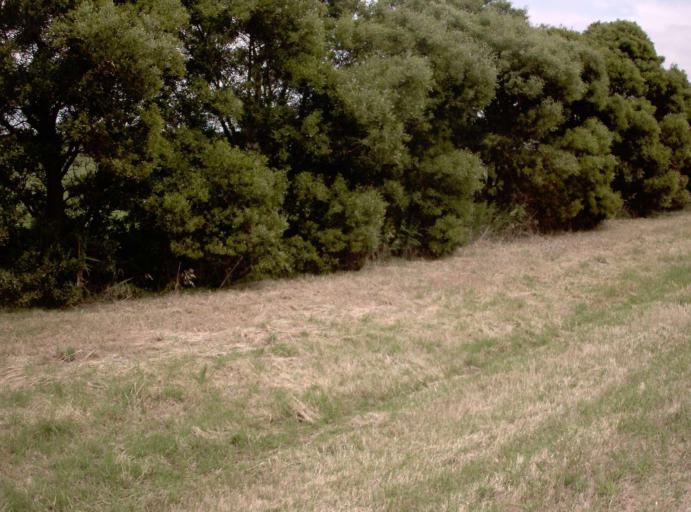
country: AU
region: Victoria
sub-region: Latrobe
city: Moe
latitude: -38.1826
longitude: 146.1473
